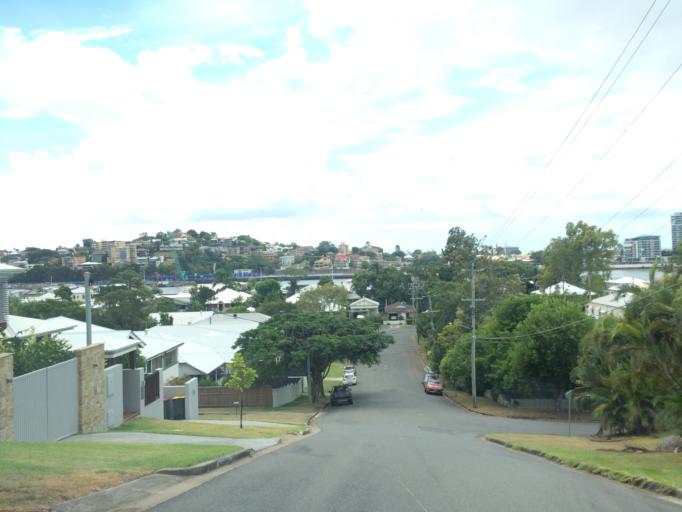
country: AU
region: Queensland
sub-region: Brisbane
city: Balmoral
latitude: -27.4459
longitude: 153.0607
